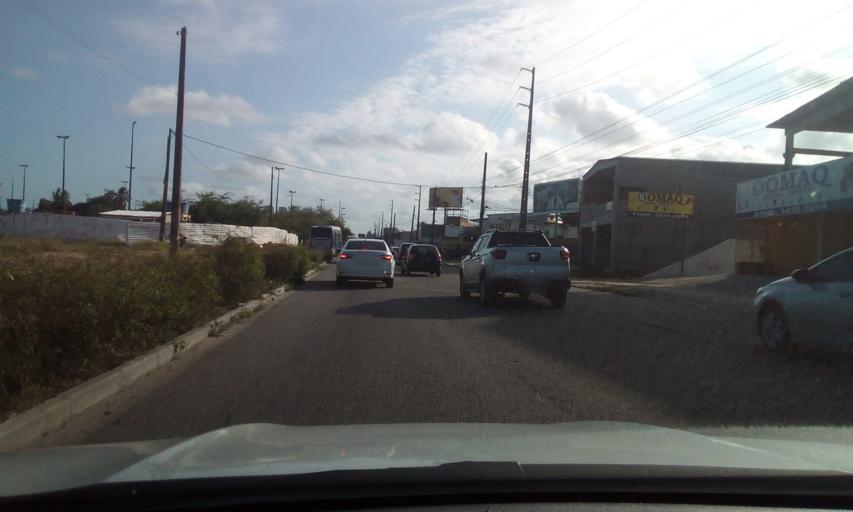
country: BR
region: Pernambuco
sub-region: Olinda
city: Olinda
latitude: -8.0273
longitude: -34.8651
